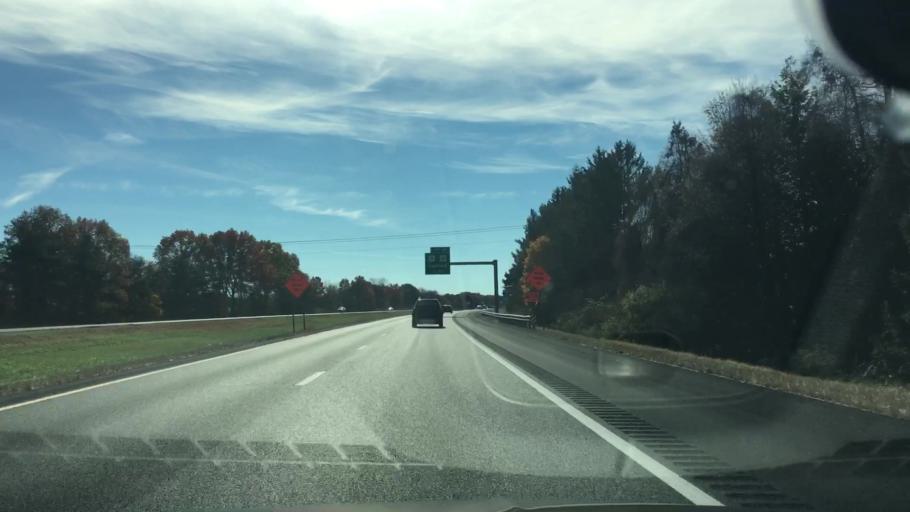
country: US
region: Massachusetts
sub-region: Hampshire County
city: Hatfield
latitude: 42.3714
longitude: -72.6335
